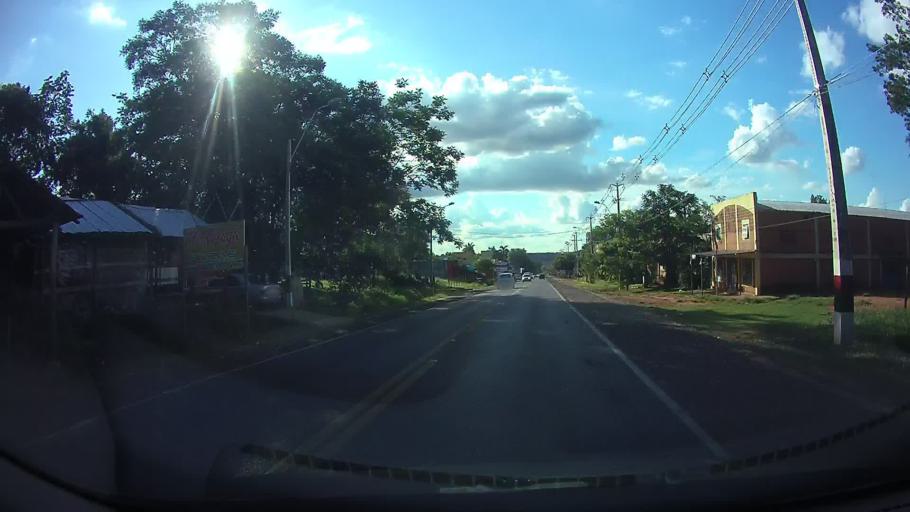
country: PY
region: Central
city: Aregua
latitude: -25.2952
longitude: -57.4330
